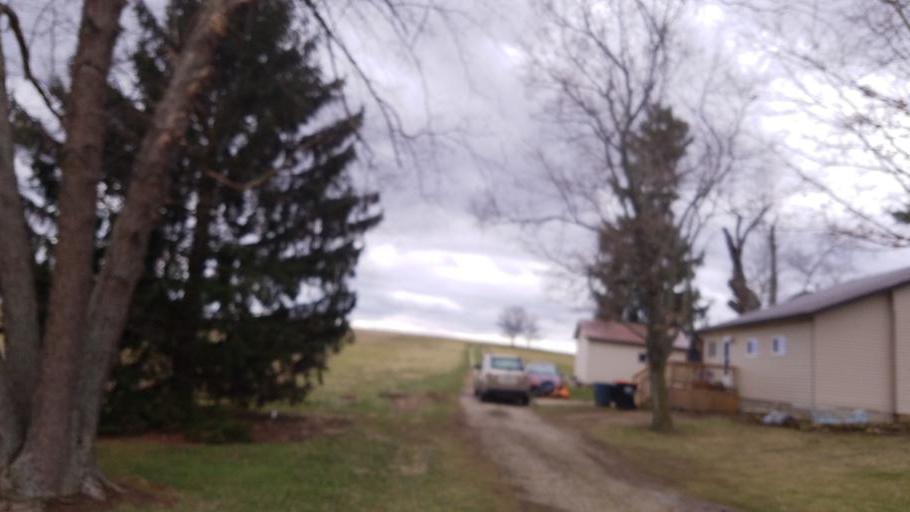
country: US
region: Ohio
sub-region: Licking County
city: Utica
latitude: 40.2261
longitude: -82.4060
